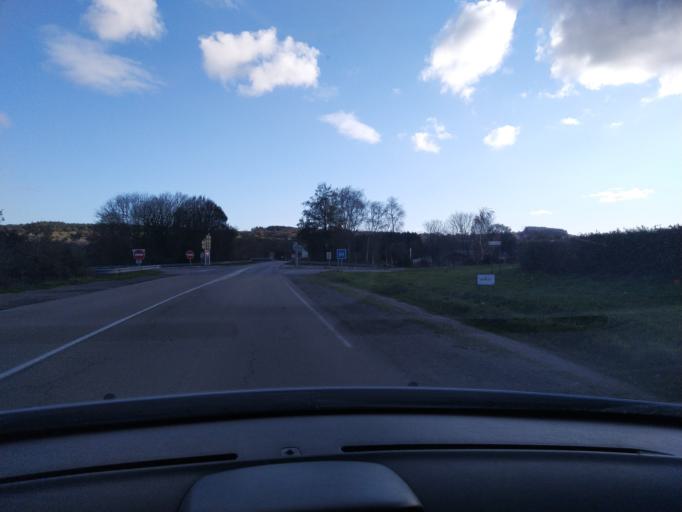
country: FR
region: Brittany
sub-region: Departement du Finistere
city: Guerlesquin
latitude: 48.5709
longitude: -3.6065
